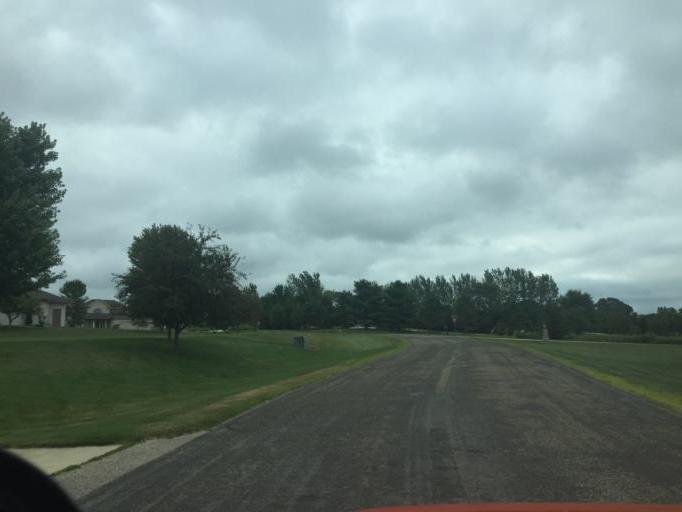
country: US
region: Minnesota
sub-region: Olmsted County
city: Rochester
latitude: 43.9671
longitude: -92.5410
